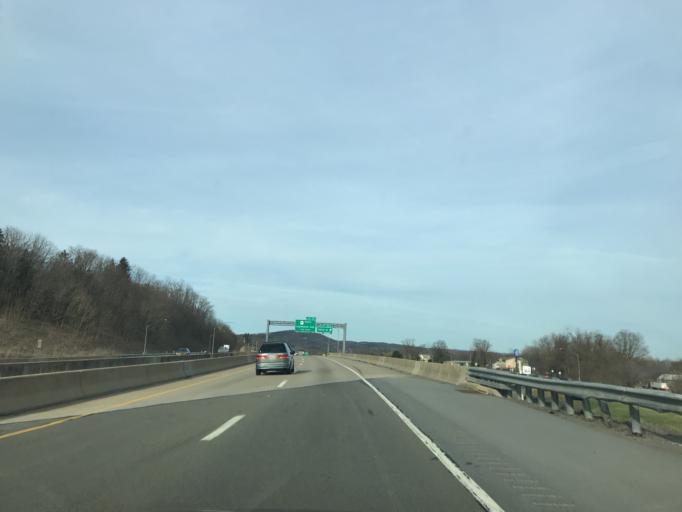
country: US
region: Pennsylvania
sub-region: Lycoming County
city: Kenmar
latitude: 41.2463
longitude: -76.9468
